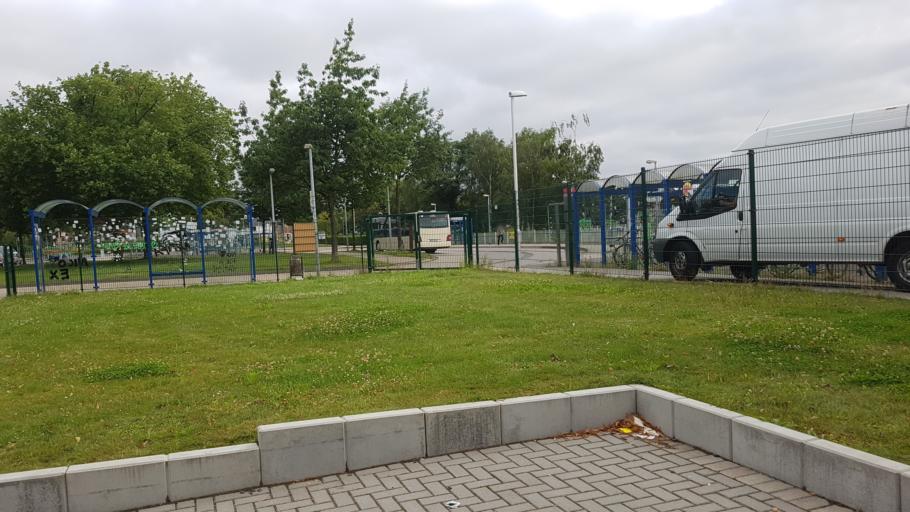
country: DE
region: North Rhine-Westphalia
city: Julich
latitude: 50.9187
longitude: 6.3677
